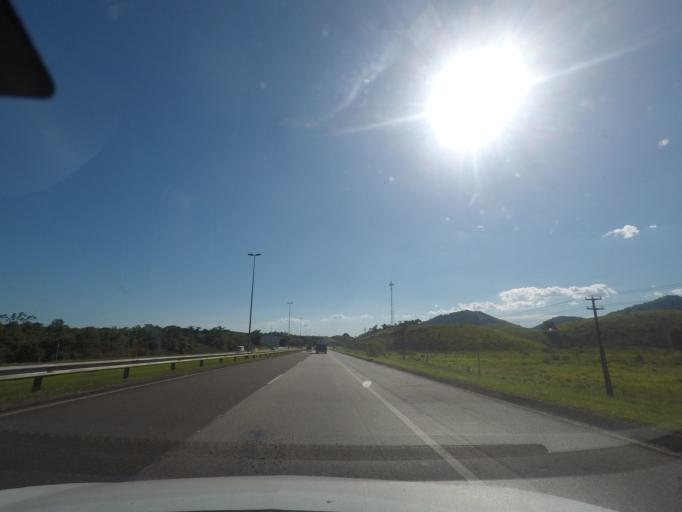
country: BR
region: Rio de Janeiro
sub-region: Guapimirim
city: Guapimirim
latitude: -22.6495
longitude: -43.0750
